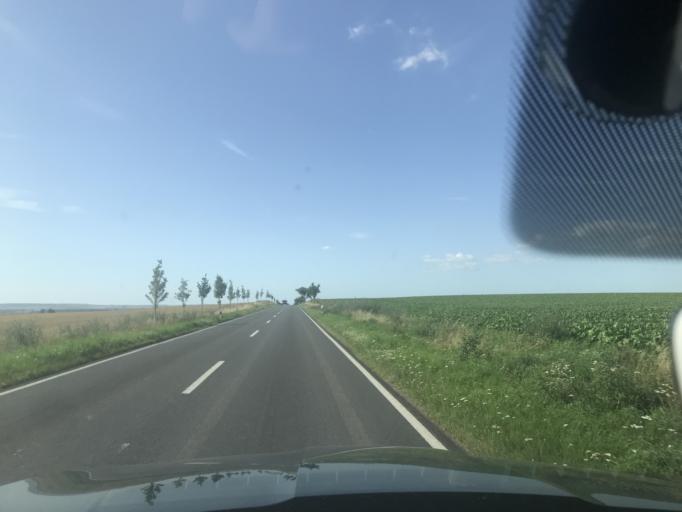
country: DE
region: Saxony-Anhalt
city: Ditfurt
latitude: 51.8488
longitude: 11.1922
